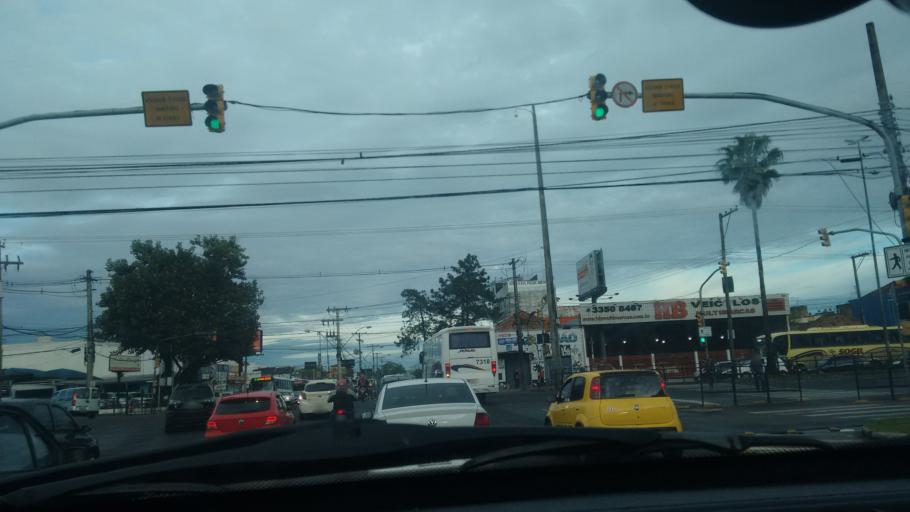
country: BR
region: Rio Grande do Sul
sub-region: Cachoeirinha
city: Cachoeirinha
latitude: -29.9999
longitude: -51.1324
